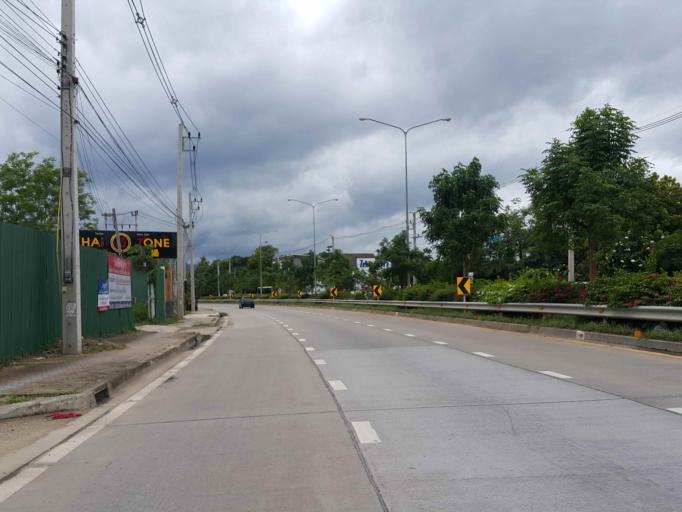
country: TH
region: Chiang Mai
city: San Sai
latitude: 18.8460
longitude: 98.9933
